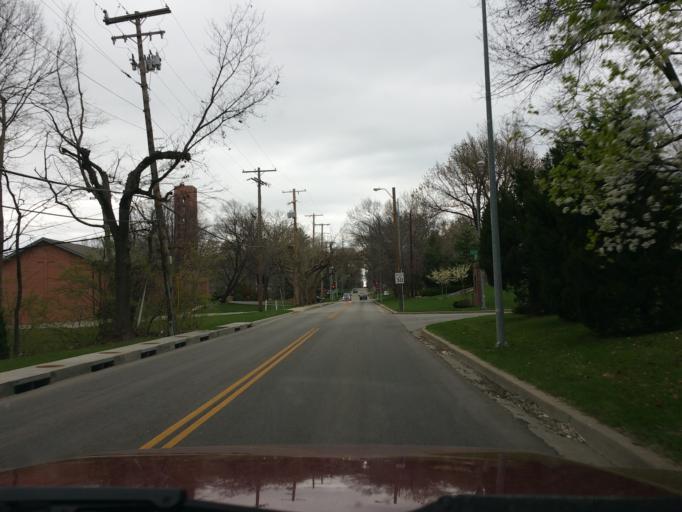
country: US
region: Kansas
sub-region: Johnson County
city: Mission Hills
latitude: 39.0124
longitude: -94.6078
